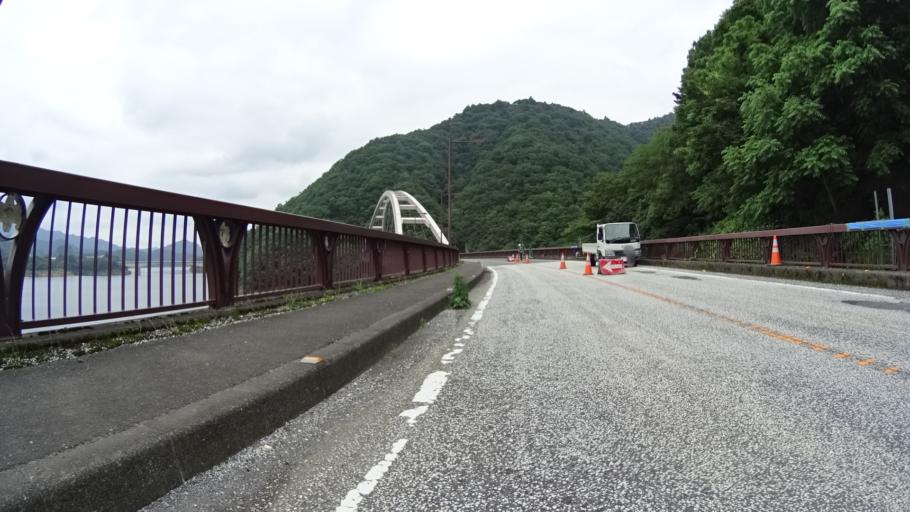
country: JP
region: Kanagawa
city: Atsugi
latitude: 35.5186
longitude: 139.2412
